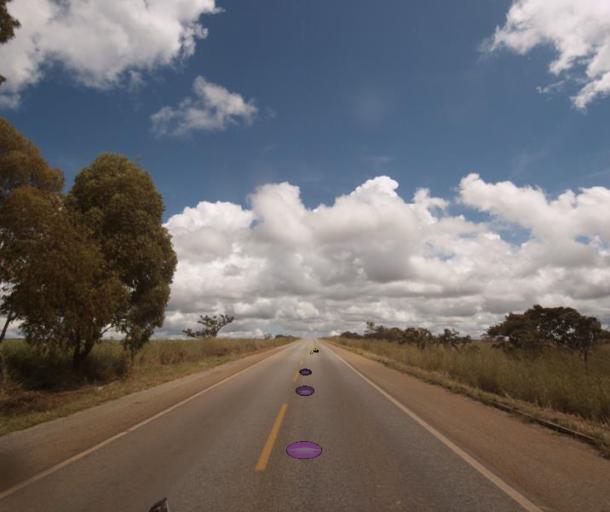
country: BR
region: Goias
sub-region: Pirenopolis
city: Pirenopolis
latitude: -15.7538
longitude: -48.6794
